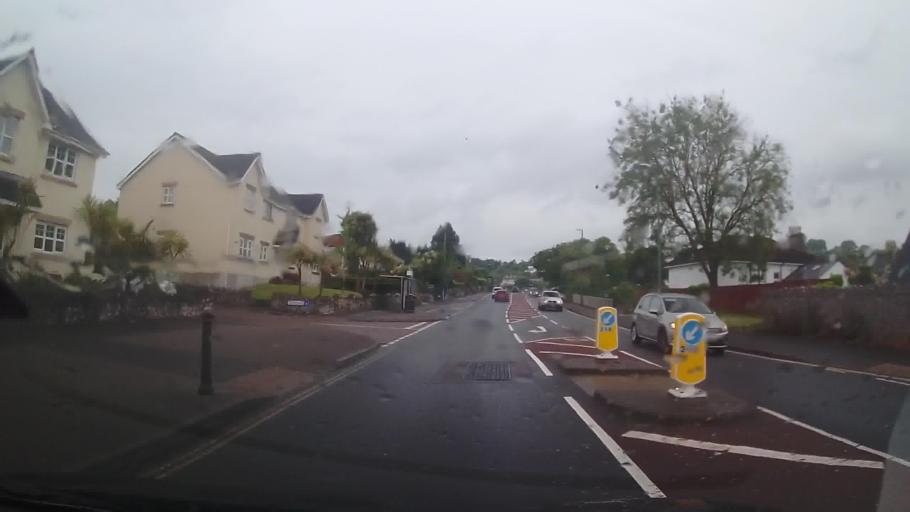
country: GB
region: England
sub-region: Borough of Torbay
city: Paignton
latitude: 50.4172
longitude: -3.5613
